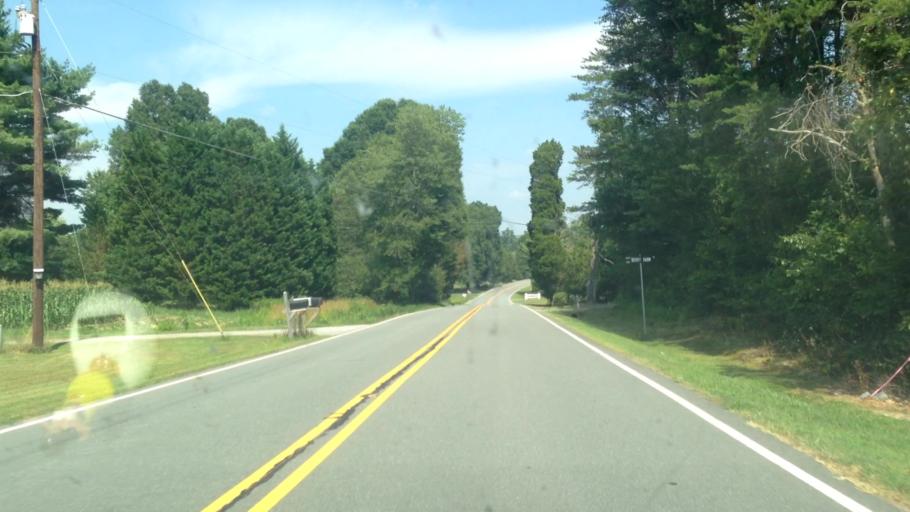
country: US
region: North Carolina
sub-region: Stokes County
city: Walnut Cove
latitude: 36.3717
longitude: -80.0780
